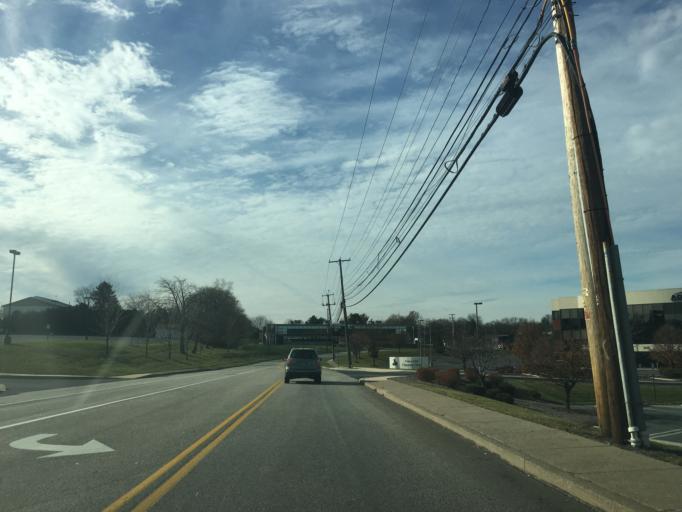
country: US
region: Pennsylvania
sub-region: Dauphin County
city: Colonial Park
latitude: 40.3066
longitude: -76.8236
